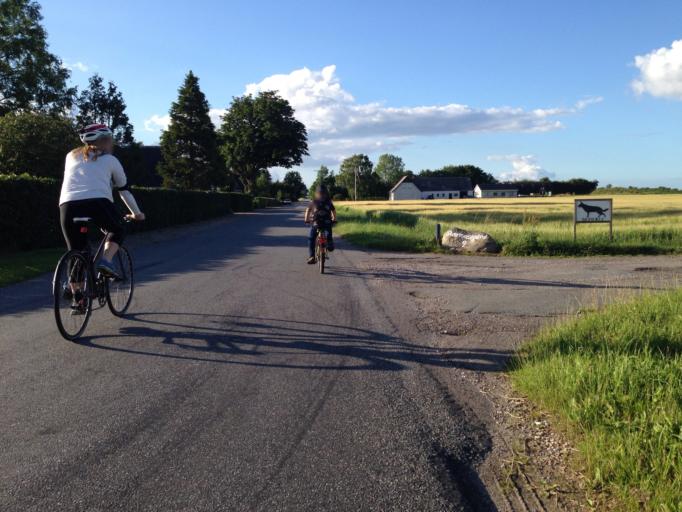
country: DK
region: South Denmark
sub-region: Middelfart Kommune
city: Norre Aby
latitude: 55.4723
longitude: 9.9035
